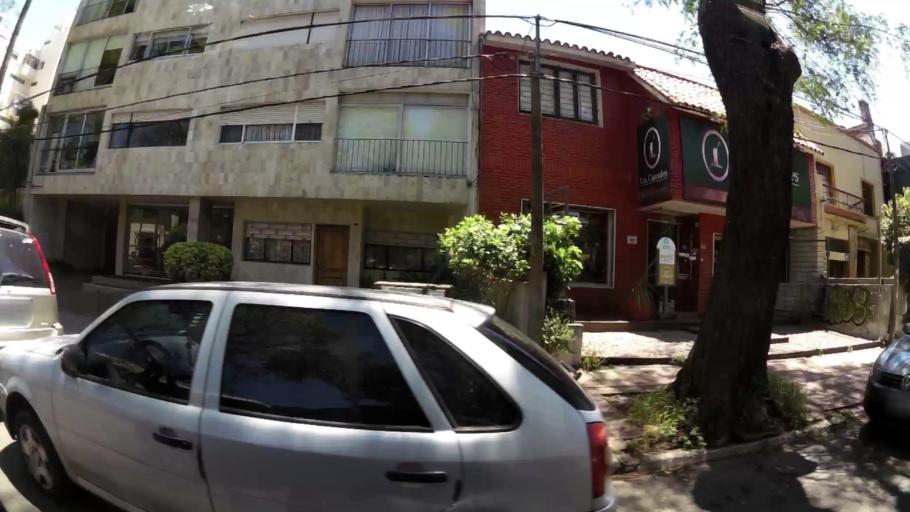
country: UY
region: Montevideo
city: Montevideo
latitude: -34.9217
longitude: -56.1580
